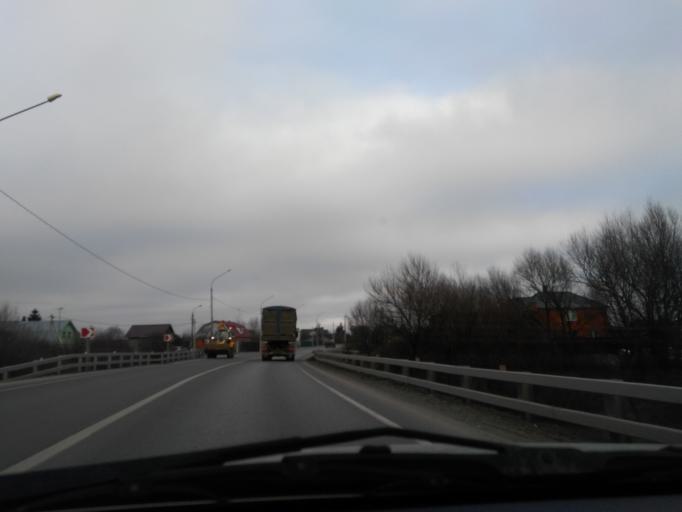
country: RU
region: Moskovskaya
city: Troitsk
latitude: 55.3706
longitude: 37.2019
